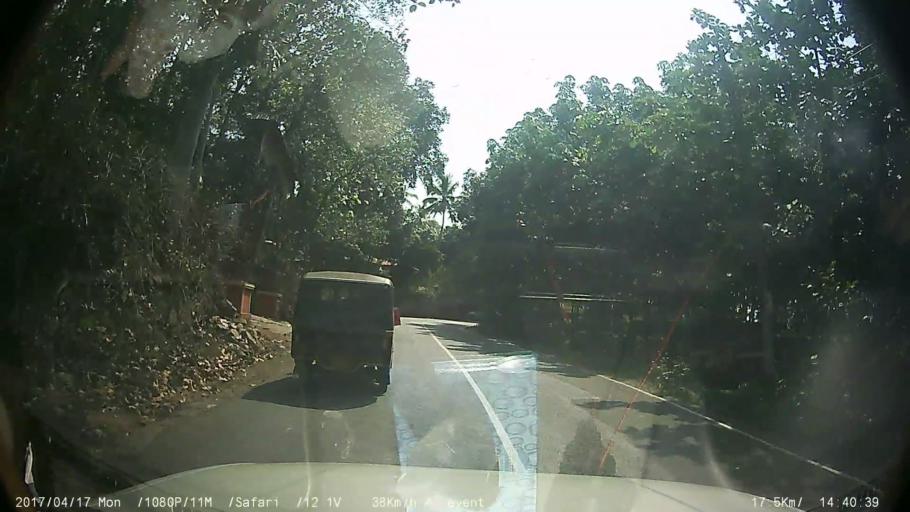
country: IN
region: Kerala
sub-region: Ernakulam
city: Piravam
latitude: 9.8315
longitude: 76.5104
